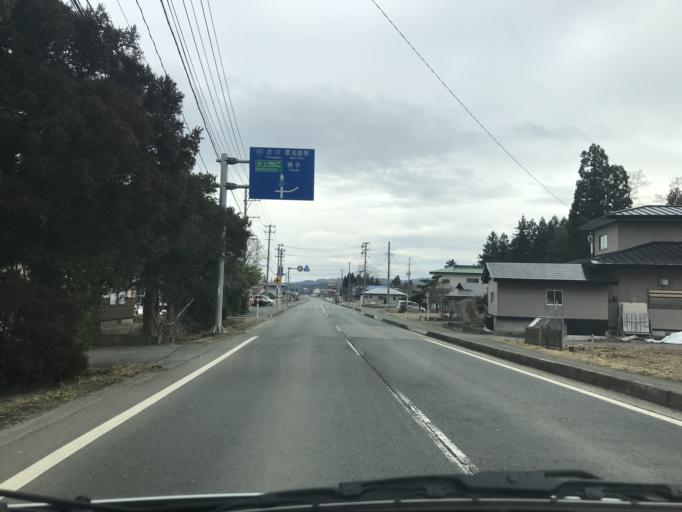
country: JP
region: Iwate
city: Kitakami
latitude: 39.3170
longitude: 140.9745
